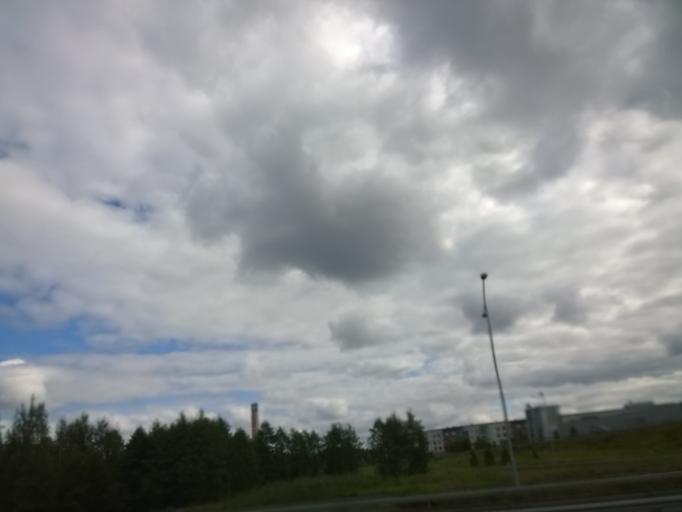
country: FI
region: Pirkanmaa
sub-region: Tampere
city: Tampere
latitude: 61.4975
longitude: 23.8819
